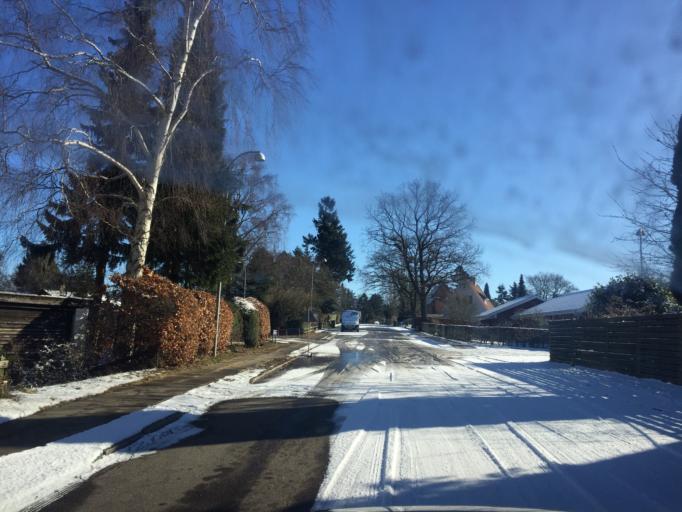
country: DK
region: Capital Region
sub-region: Herlev Kommune
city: Herlev
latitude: 55.7561
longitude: 12.4195
